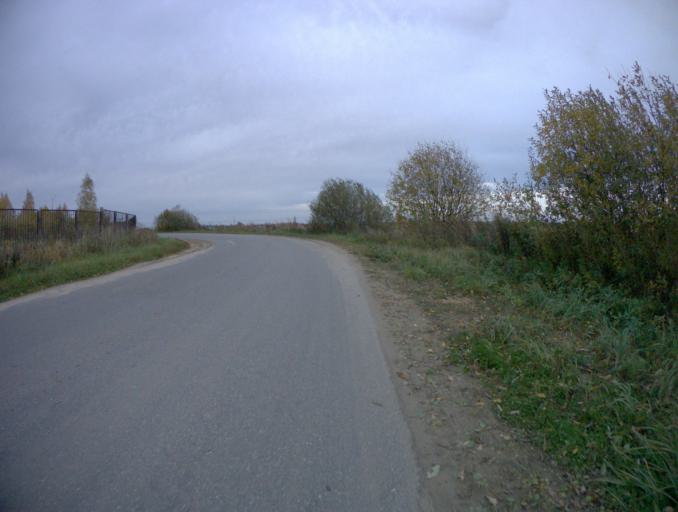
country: RU
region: Vladimir
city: Kommunar
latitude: 56.0527
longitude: 40.4867
